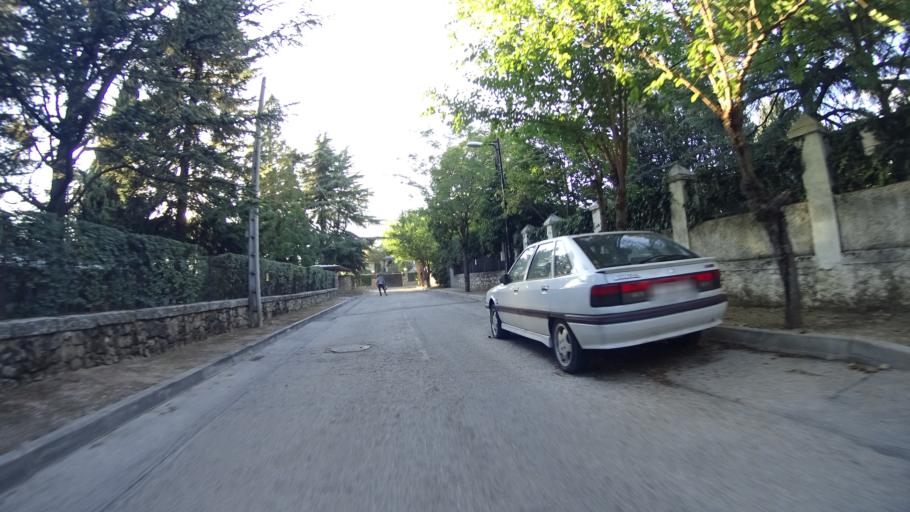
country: ES
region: Madrid
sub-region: Provincia de Madrid
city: Torrelodones
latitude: 40.5838
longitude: -3.9579
